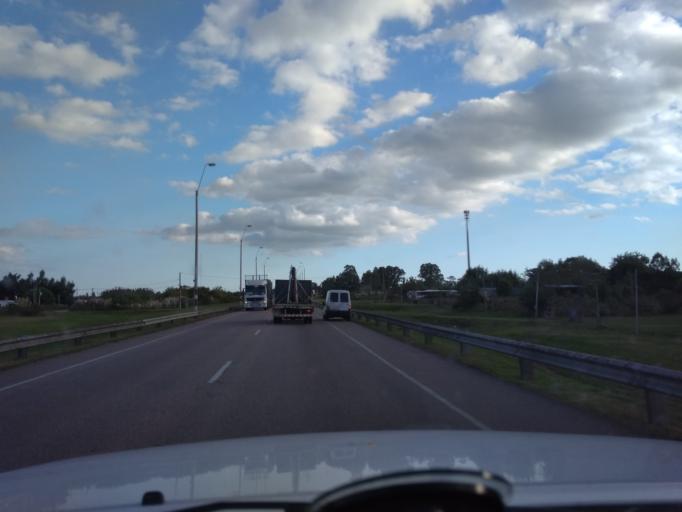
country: UY
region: Canelones
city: Canelones
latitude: -34.5384
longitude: -56.2732
